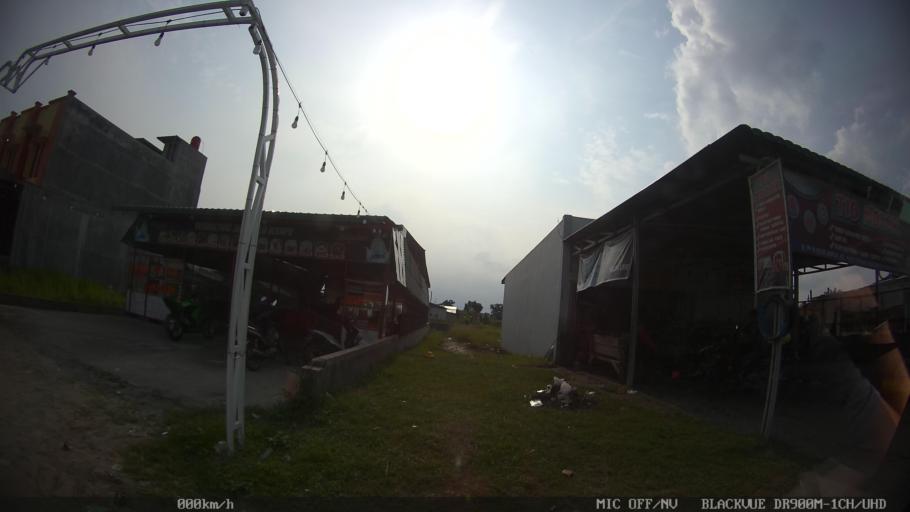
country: ID
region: North Sumatra
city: Medan
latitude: 3.5766
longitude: 98.7565
